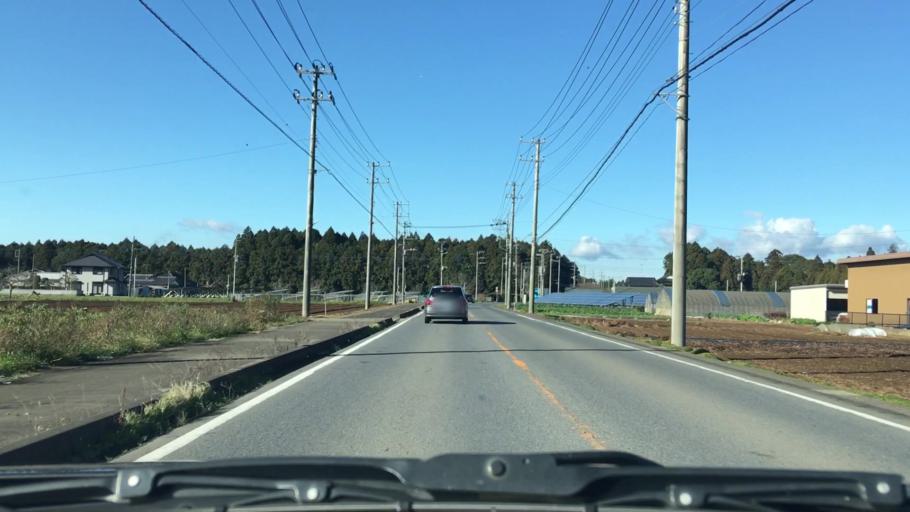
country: JP
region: Chiba
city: Sawara
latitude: 35.8374
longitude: 140.5498
